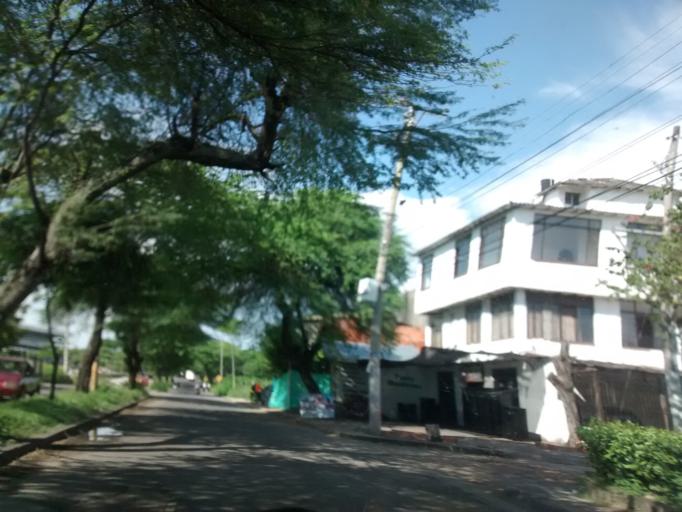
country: CO
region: Cundinamarca
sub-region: Girardot
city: Girardot City
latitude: 4.3091
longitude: -74.7936
